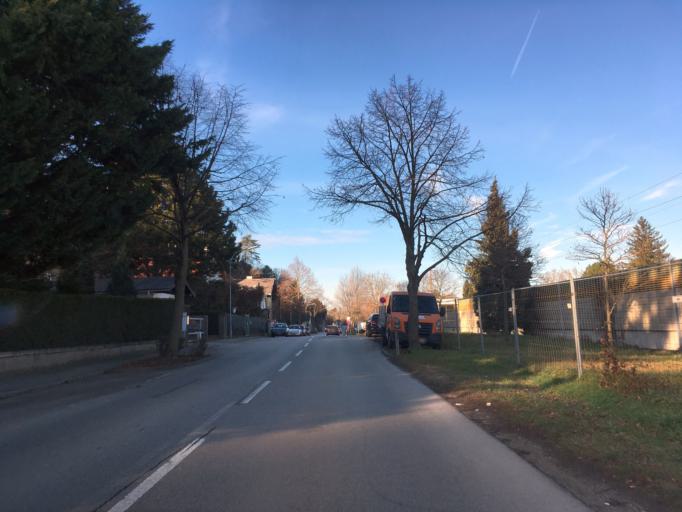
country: AT
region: Lower Austria
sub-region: Politischer Bezirk Korneuburg
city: Korneuburg
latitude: 48.3439
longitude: 16.2918
